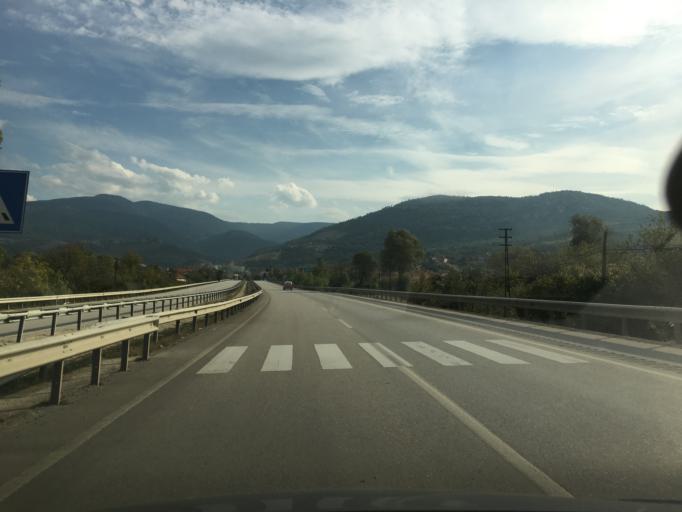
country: TR
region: Karabuk
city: Karabuk
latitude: 41.1087
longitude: 32.6686
